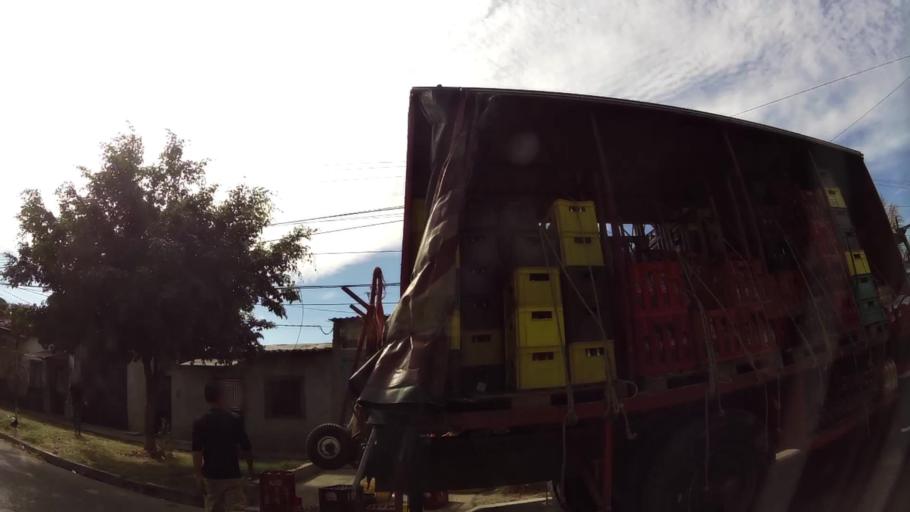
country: SV
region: Santa Ana
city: Chalchuapa
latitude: 13.9823
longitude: -89.6738
